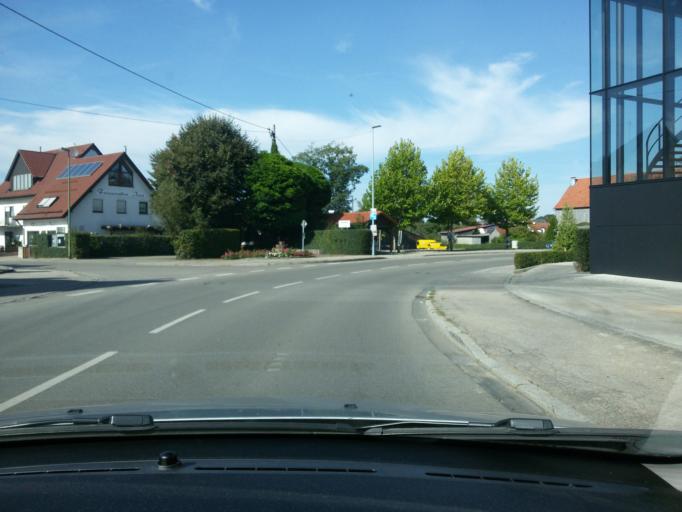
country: DE
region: Bavaria
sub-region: Swabia
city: Ustersbach
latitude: 48.3155
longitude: 10.6403
